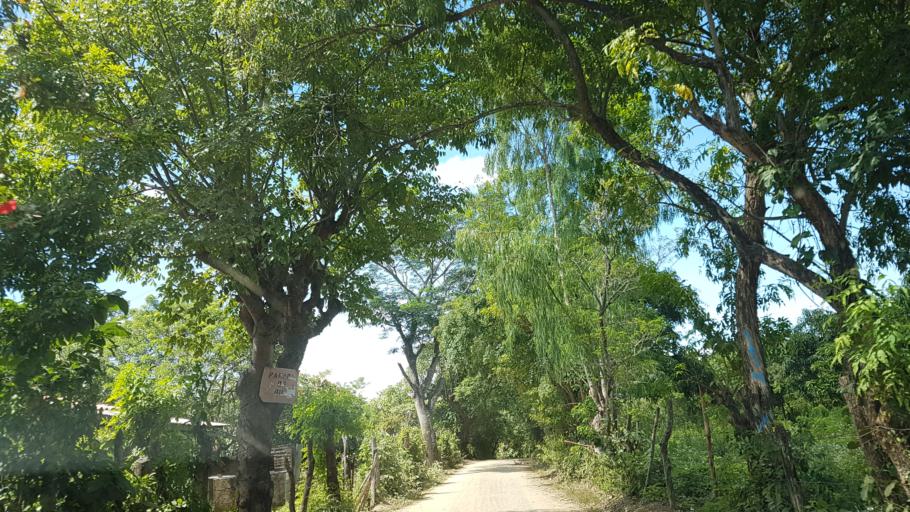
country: HN
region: El Paraiso
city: Oropoli
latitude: 13.7367
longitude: -86.6982
